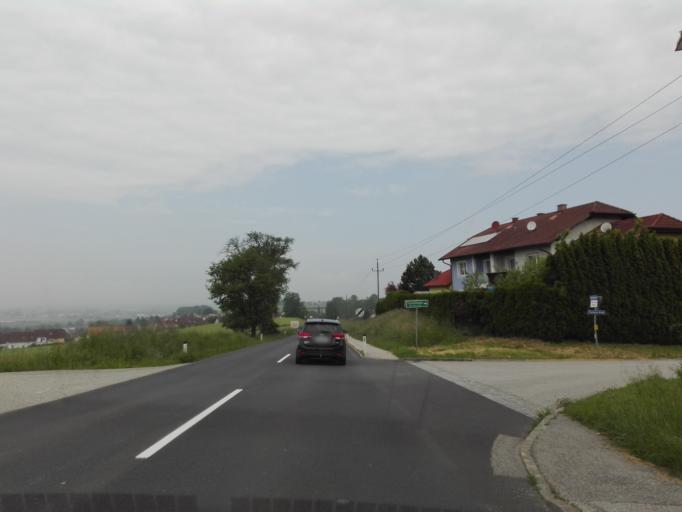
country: AT
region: Upper Austria
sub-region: Politischer Bezirk Linz-Land
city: Pasching
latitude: 48.2782
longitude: 14.1633
